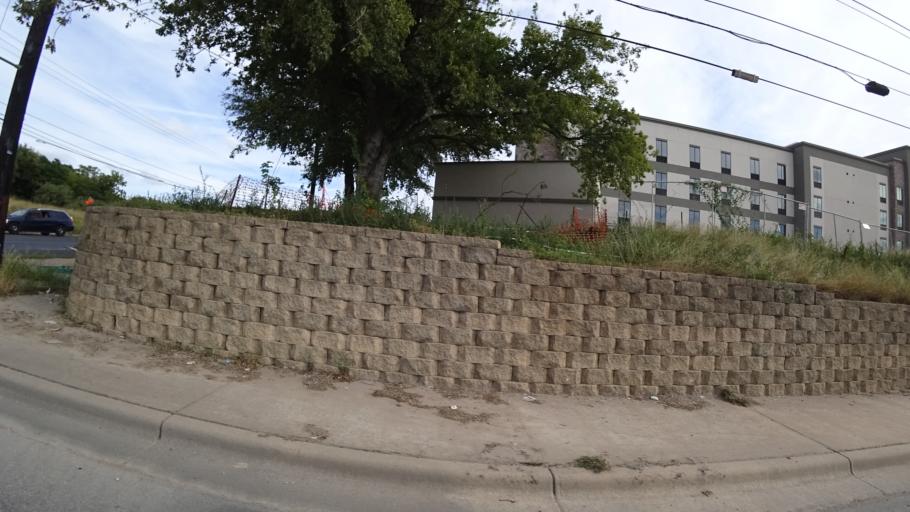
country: US
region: Texas
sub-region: Travis County
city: Austin
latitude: 30.2052
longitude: -97.7580
